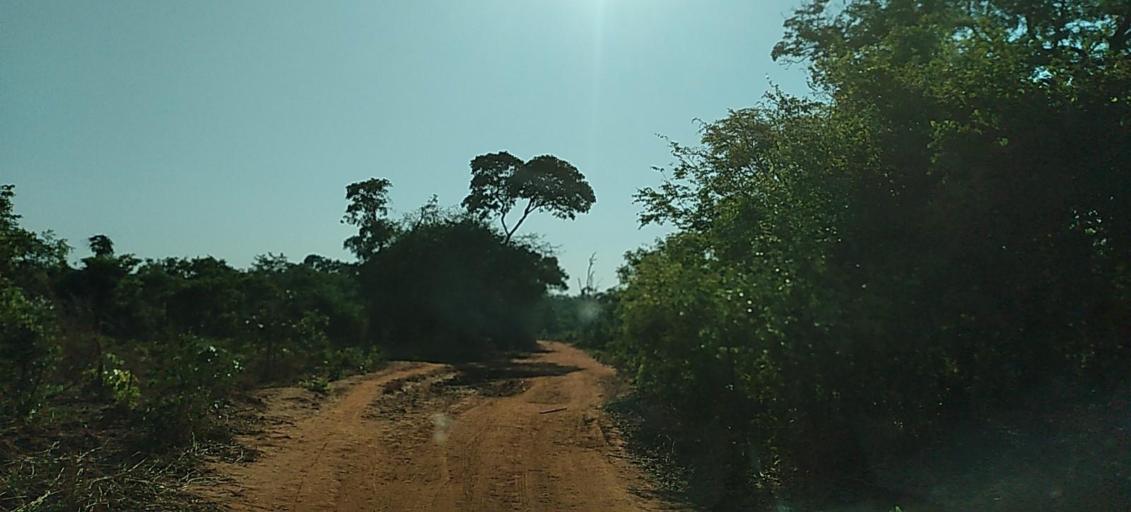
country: ZM
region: Copperbelt
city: Luanshya
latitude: -13.4590
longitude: 28.8201
